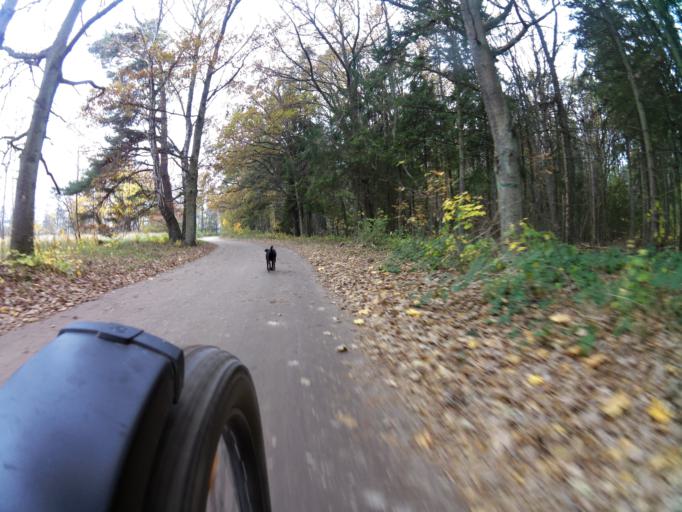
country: PL
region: Pomeranian Voivodeship
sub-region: Powiat pucki
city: Krokowa
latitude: 54.8291
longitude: 18.1330
